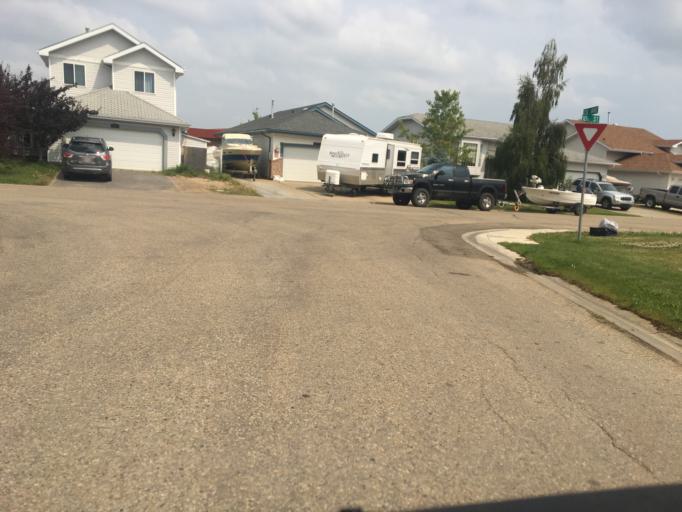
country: CA
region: Alberta
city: Grande Prairie
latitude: 55.1502
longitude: -118.8134
